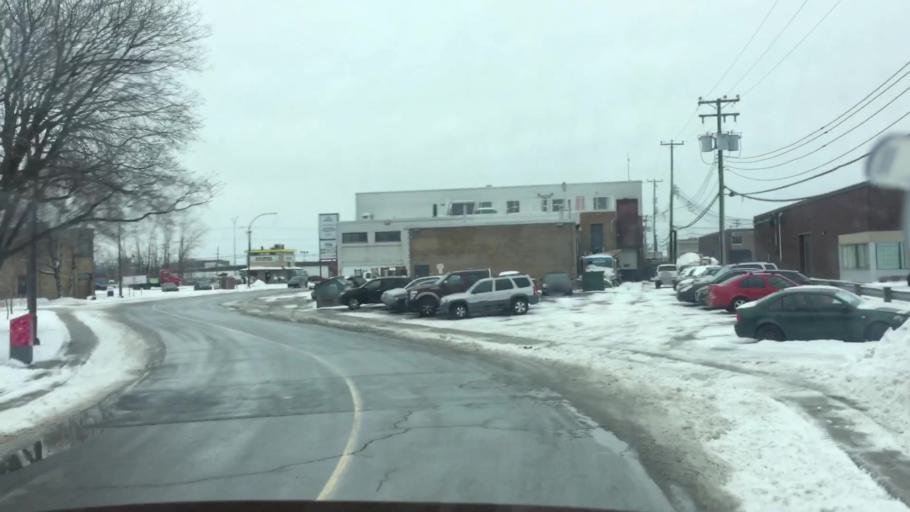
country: CA
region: Quebec
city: Dorval
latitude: 45.4606
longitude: -73.7212
